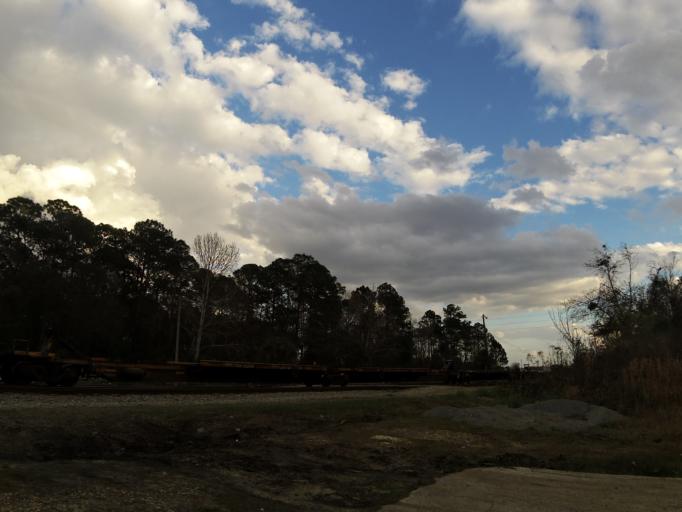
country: US
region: Florida
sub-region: Duval County
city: Jacksonville
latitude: 30.2617
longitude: -81.6183
